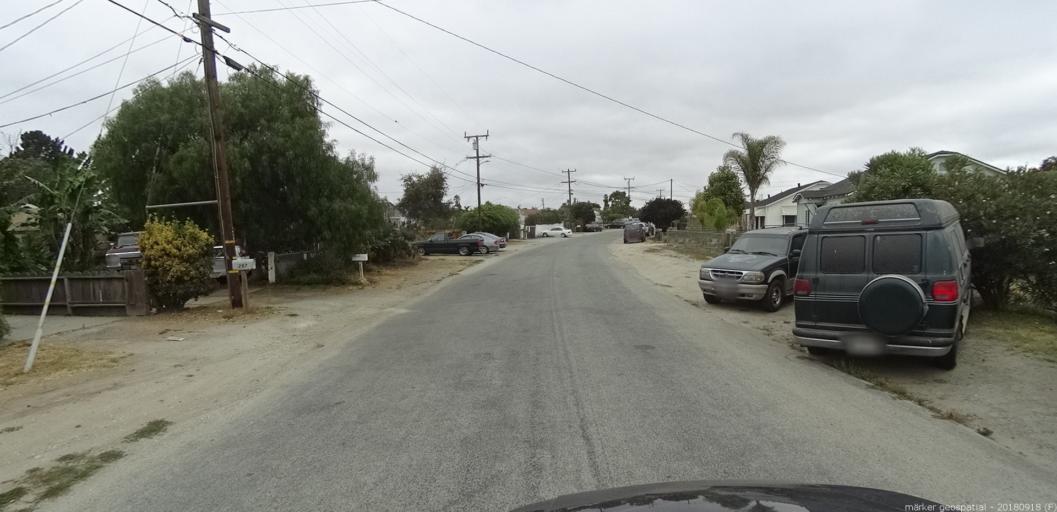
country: US
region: California
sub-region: Monterey County
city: Boronda
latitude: 36.7326
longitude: -121.6421
